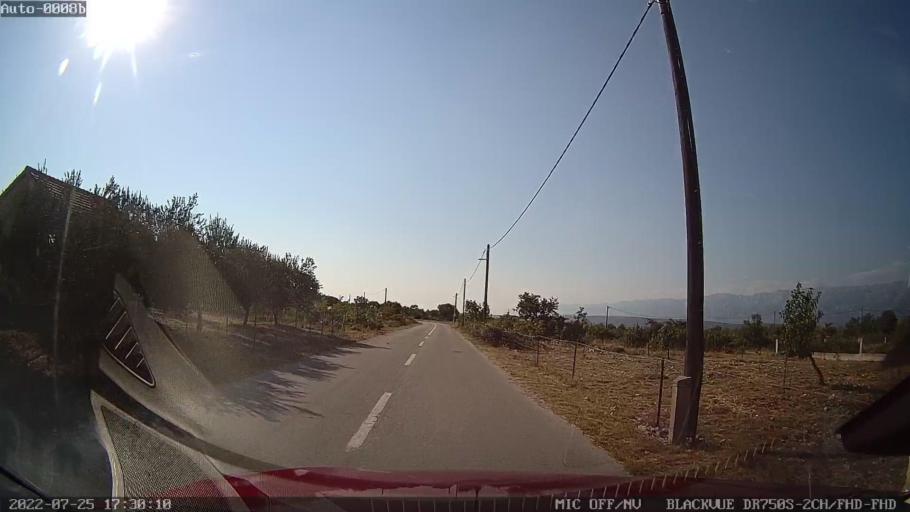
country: HR
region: Zadarska
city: Pridraga
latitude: 44.1633
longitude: 15.5112
